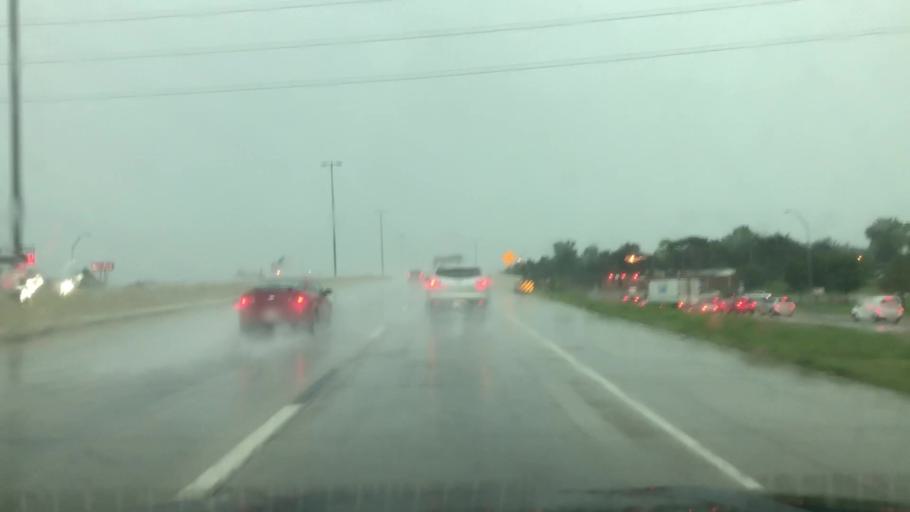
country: US
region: Oklahoma
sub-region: Tulsa County
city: Jenks
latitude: 36.0970
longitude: -95.9202
